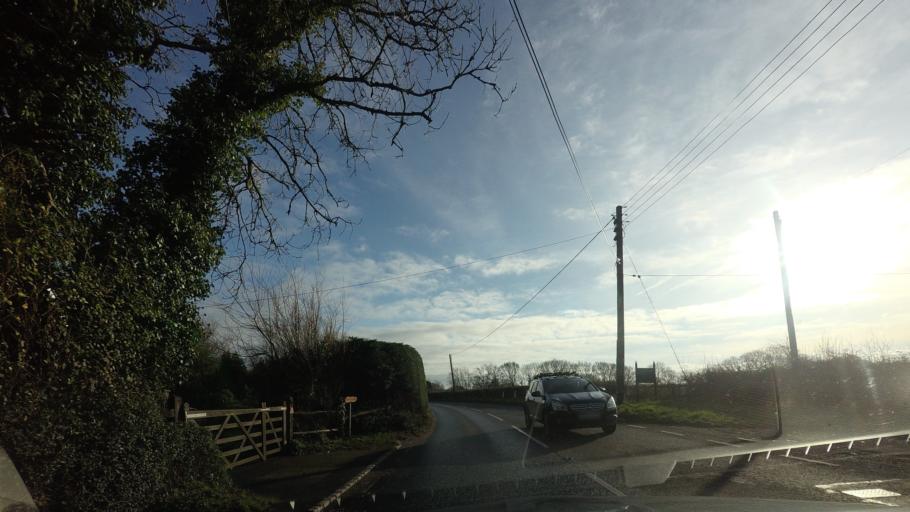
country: GB
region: England
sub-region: East Sussex
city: Bexhill-on-Sea
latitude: 50.8749
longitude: 0.4315
